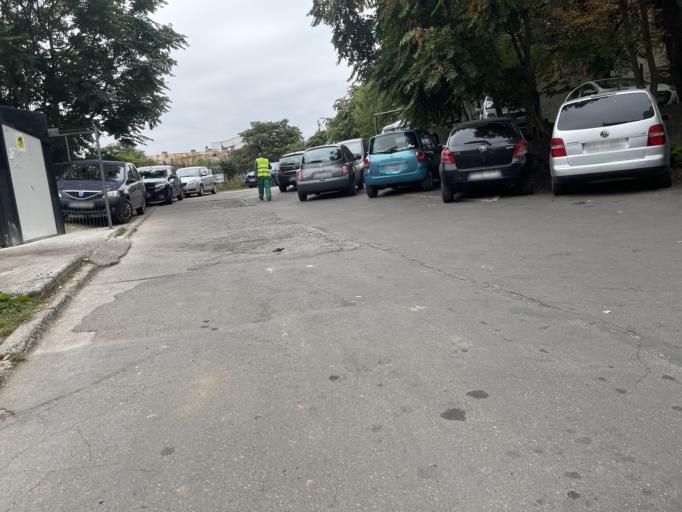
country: RO
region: Iasi
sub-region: Municipiul Iasi
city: Iasi
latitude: 47.1636
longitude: 27.5801
